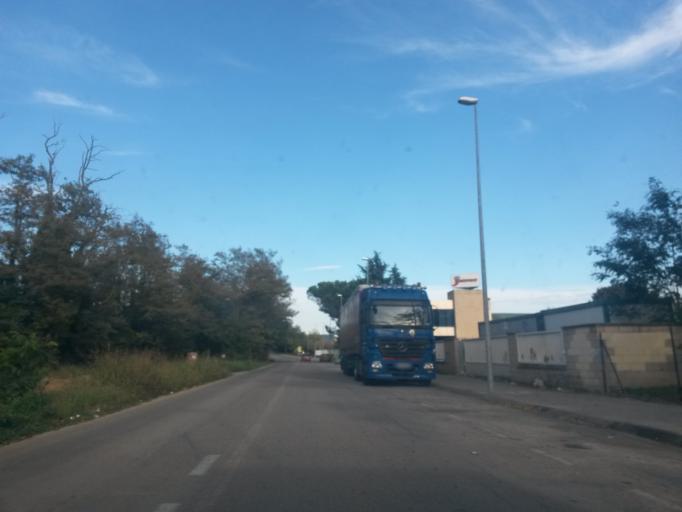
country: ES
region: Catalonia
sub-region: Provincia de Girona
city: Vilablareix
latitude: 41.9706
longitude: 2.7736
